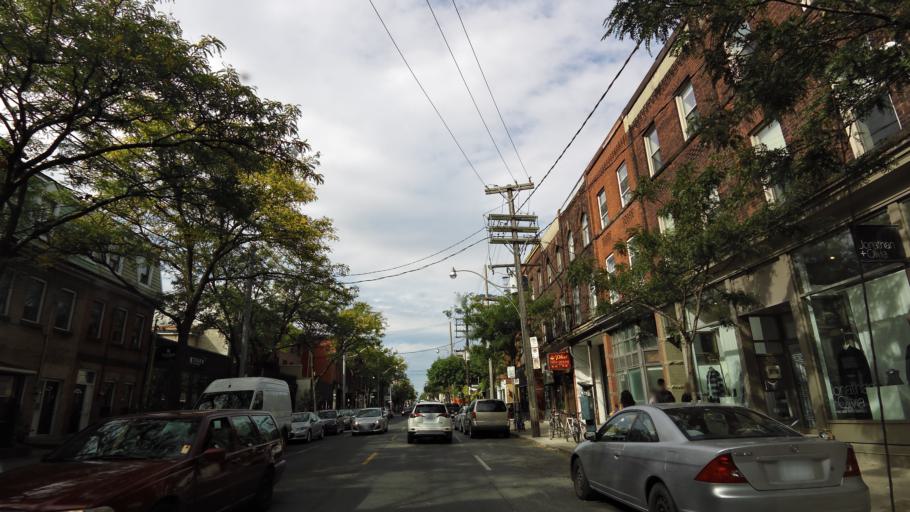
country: CA
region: Ontario
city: Toronto
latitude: 43.6451
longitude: -79.4193
